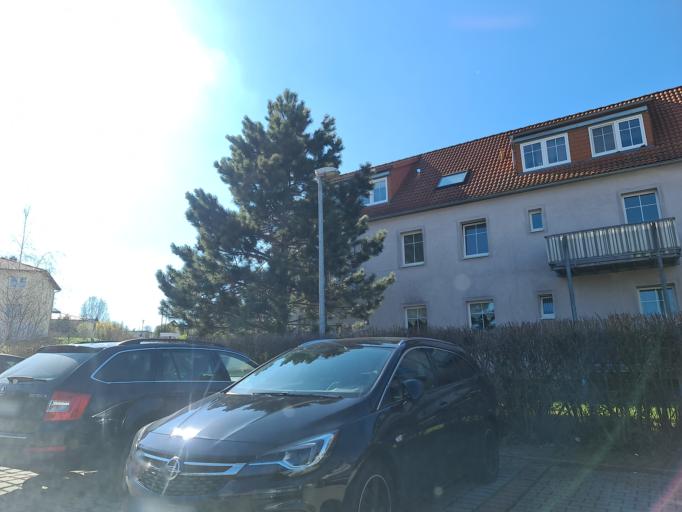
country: DE
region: Saxony
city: Plauen
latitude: 50.4958
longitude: 12.0999
